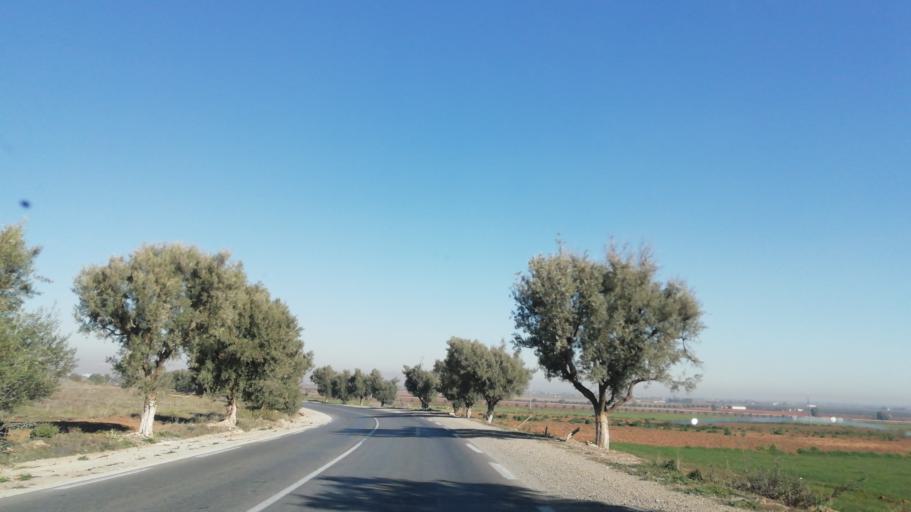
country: DZ
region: Mascara
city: Mascara
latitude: 35.2624
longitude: 0.1288
